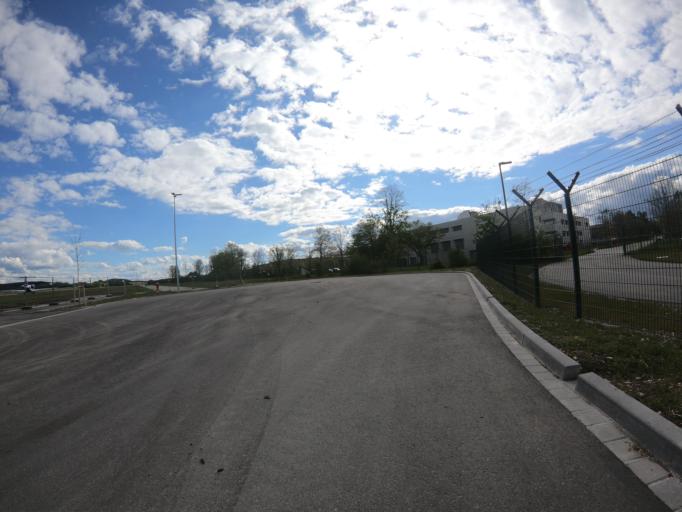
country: DE
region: Bavaria
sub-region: Upper Bavaria
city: Gilching
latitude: 48.0861
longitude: 11.2823
